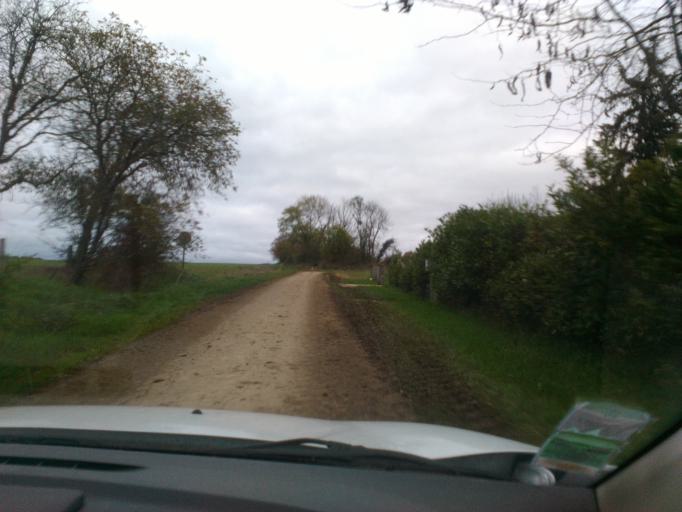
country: FR
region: Lorraine
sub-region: Departement des Vosges
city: Mirecourt
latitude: 48.2828
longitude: 6.1979
